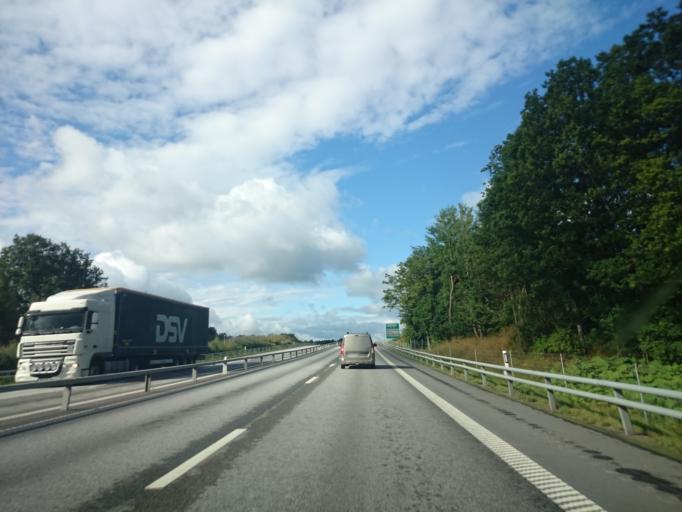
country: SE
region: Skane
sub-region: Horby Kommun
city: Hoerby
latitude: 55.9158
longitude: 13.7759
